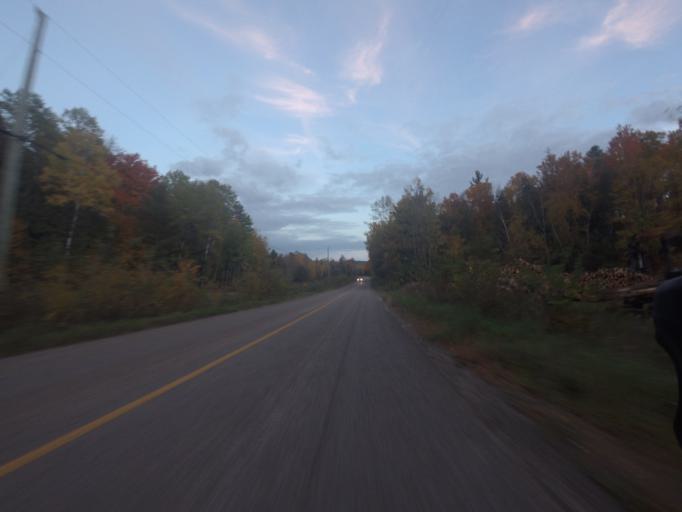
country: CA
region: Ontario
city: Renfrew
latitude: 45.3535
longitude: -76.9516
